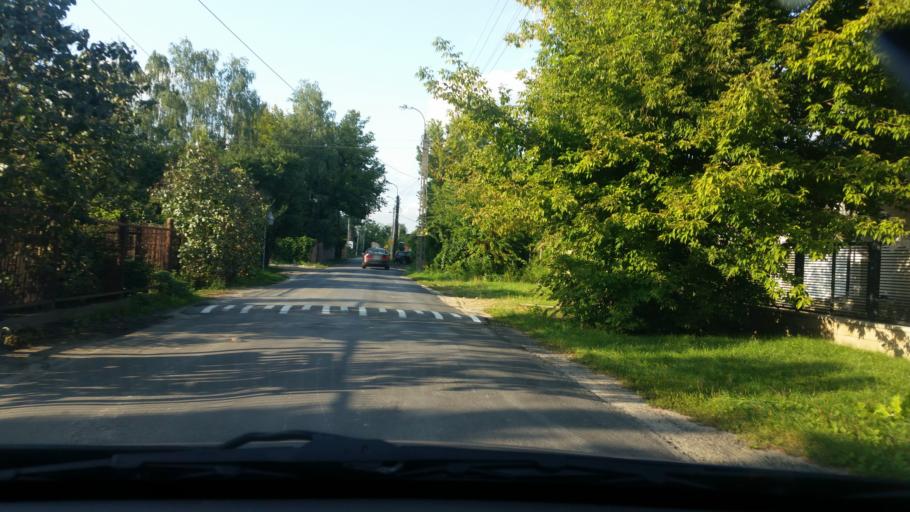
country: PL
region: Masovian Voivodeship
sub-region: Warszawa
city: Bemowo
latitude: 52.2441
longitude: 20.8861
